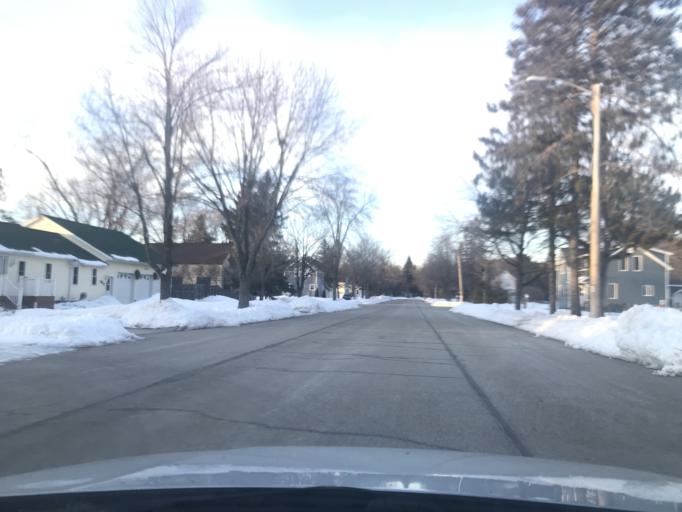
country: US
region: Wisconsin
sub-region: Marinette County
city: Peshtigo
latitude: 45.0570
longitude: -87.7402
